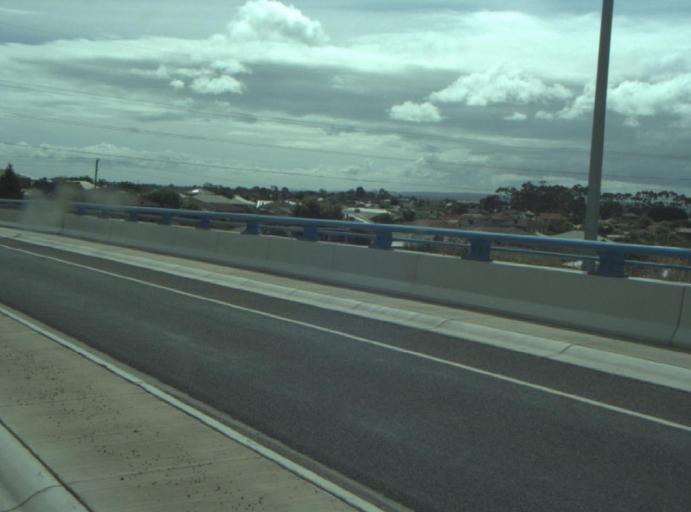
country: AU
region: Victoria
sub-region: Greater Geelong
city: Wandana Heights
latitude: -38.1894
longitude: 144.3079
